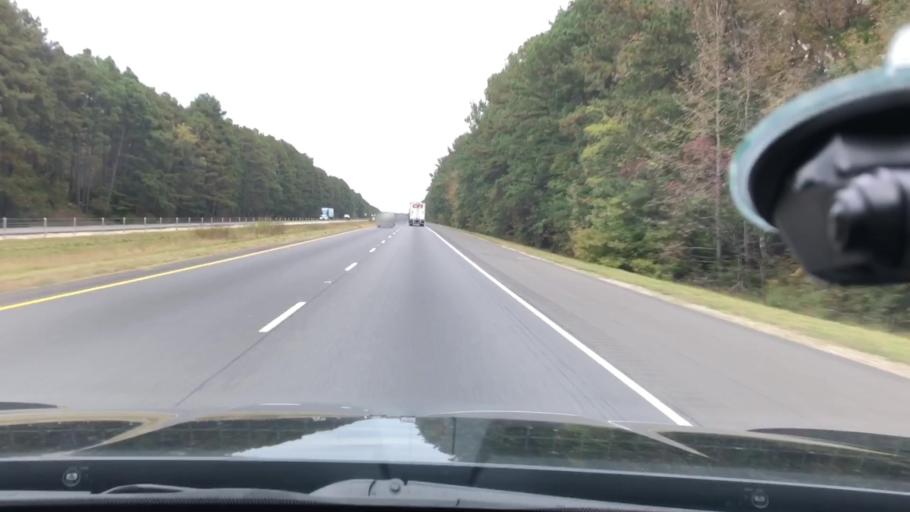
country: US
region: Arkansas
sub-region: Clark County
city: Arkadelphia
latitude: 34.2737
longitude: -92.9680
